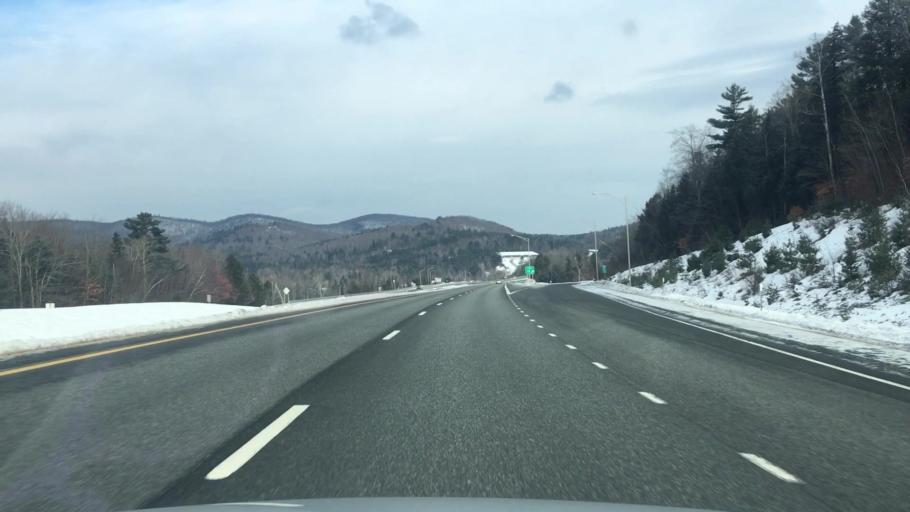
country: US
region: New Hampshire
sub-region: Sullivan County
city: Grantham
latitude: 43.4946
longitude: -72.1310
